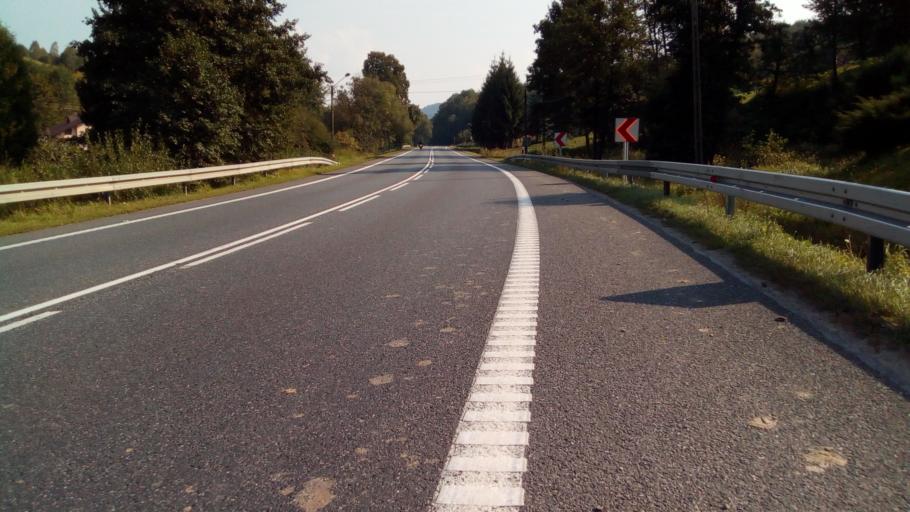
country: PL
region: Subcarpathian Voivodeship
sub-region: Powiat strzyzowski
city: Jawornik
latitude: 49.8185
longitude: 21.8743
